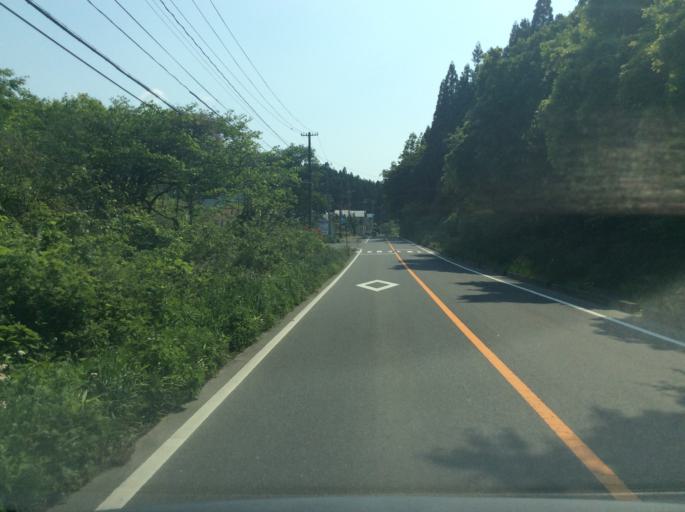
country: JP
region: Tochigi
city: Kuroiso
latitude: 37.0935
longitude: 140.2264
